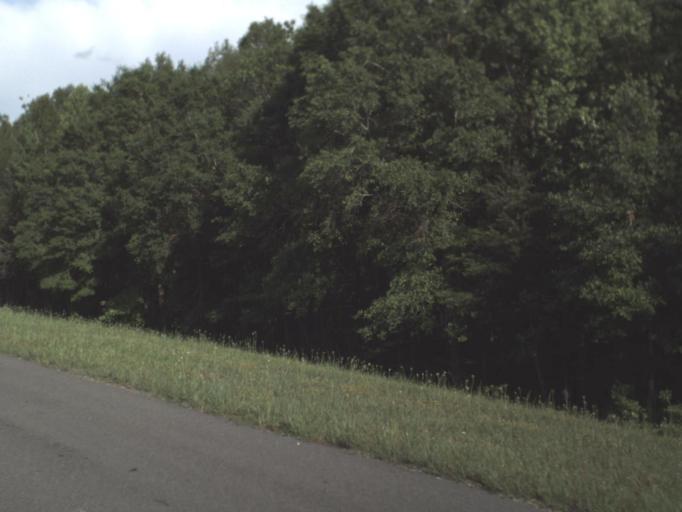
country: US
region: Florida
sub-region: Holmes County
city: Bonifay
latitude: 30.7539
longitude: -85.8411
